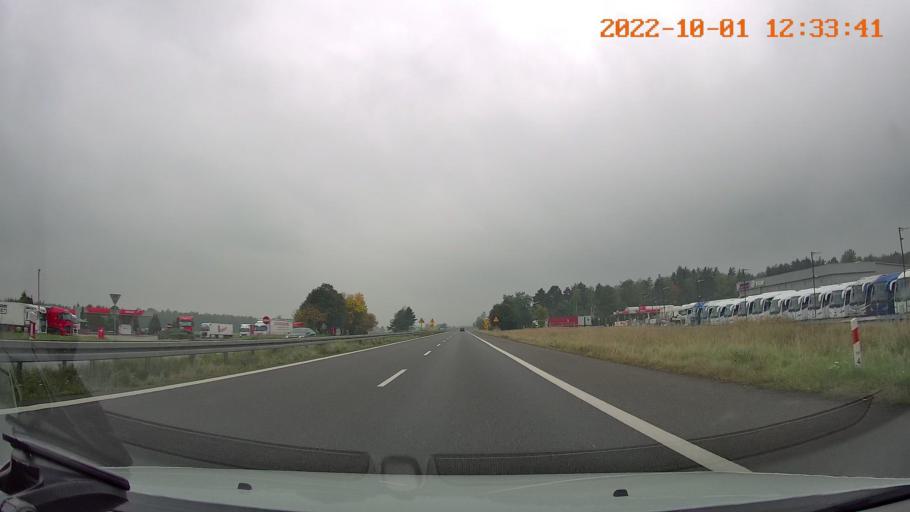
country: PL
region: Silesian Voivodeship
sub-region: Powiat bierunsko-ledzinski
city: Ledziny
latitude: 50.1473
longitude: 19.1081
